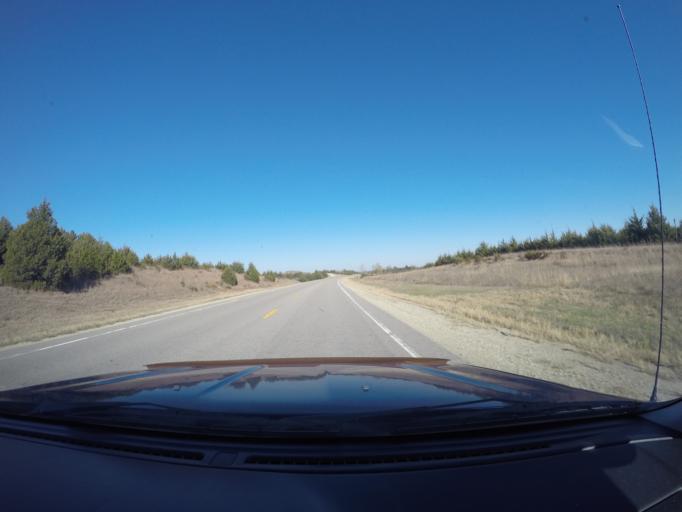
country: US
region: Kansas
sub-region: Riley County
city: Manhattan
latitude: 39.4035
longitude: -96.7639
